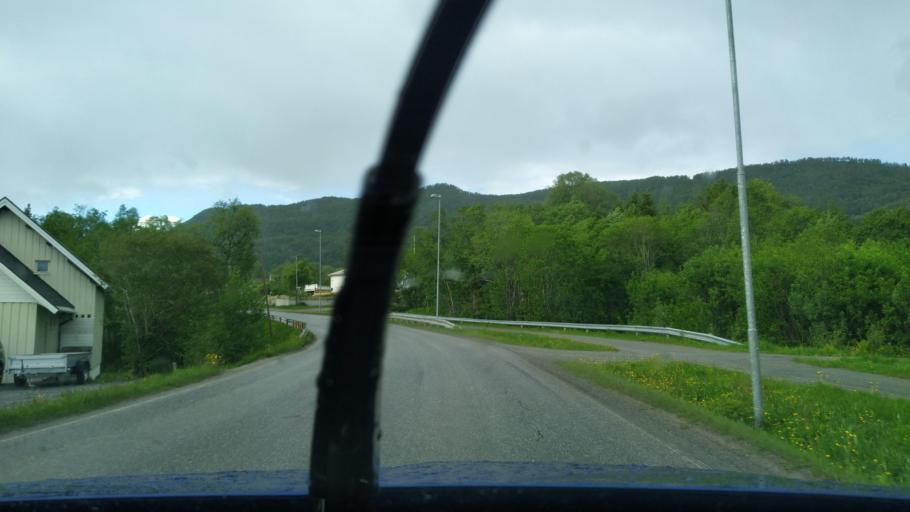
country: NO
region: Troms
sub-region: Sorreisa
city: Sorreisa
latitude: 69.1505
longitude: 18.1705
